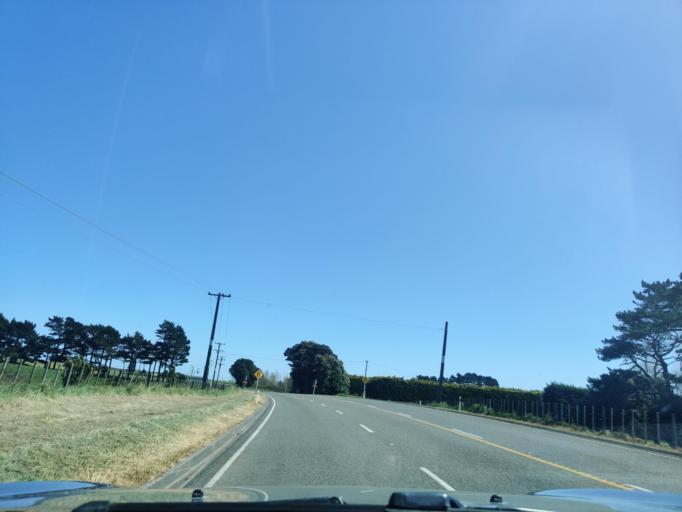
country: NZ
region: Taranaki
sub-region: South Taranaki District
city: Patea
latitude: -39.8015
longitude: 174.7234
